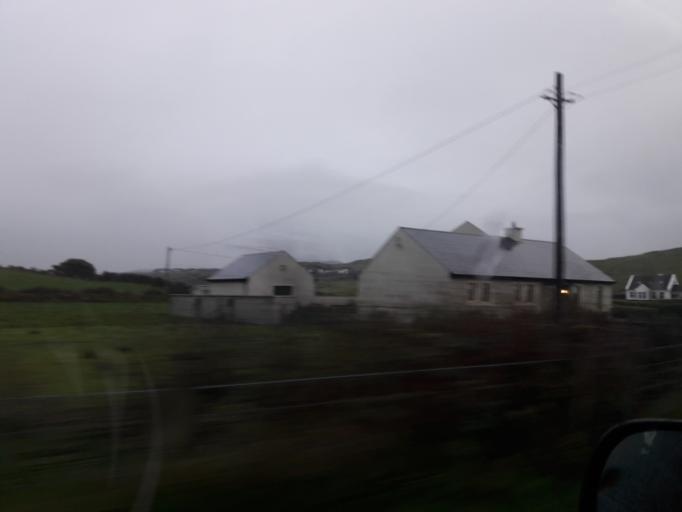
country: IE
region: Ulster
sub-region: County Donegal
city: Ramelton
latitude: 55.2593
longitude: -7.6706
